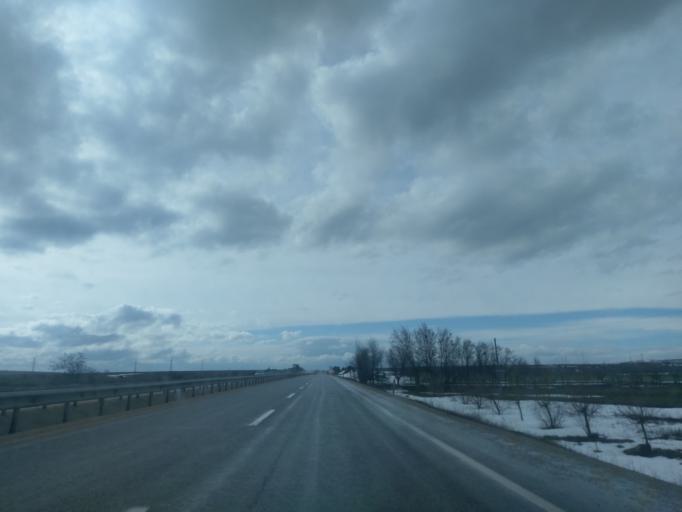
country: TR
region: Eskisehir
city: Inonu
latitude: 39.7225
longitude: 30.2518
